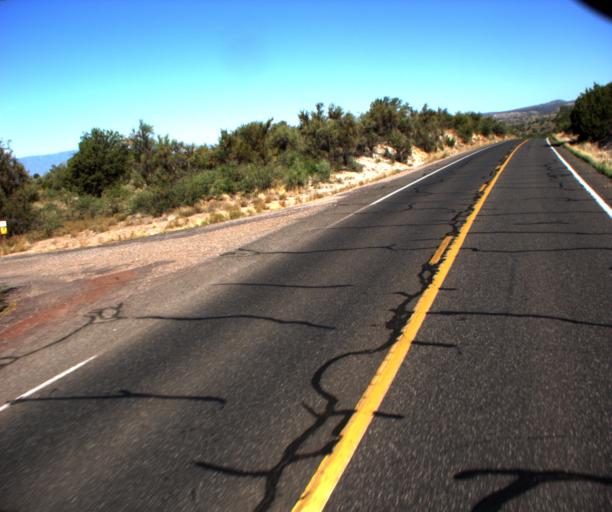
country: US
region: Arizona
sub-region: Yavapai County
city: Lake Montezuma
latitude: 34.7016
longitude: -111.7668
